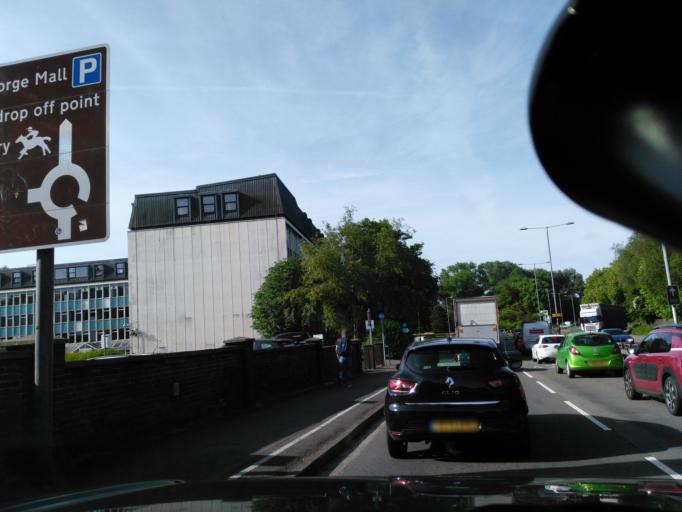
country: GB
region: England
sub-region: Wiltshire
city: Salisbury
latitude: 51.0654
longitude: -1.7888
